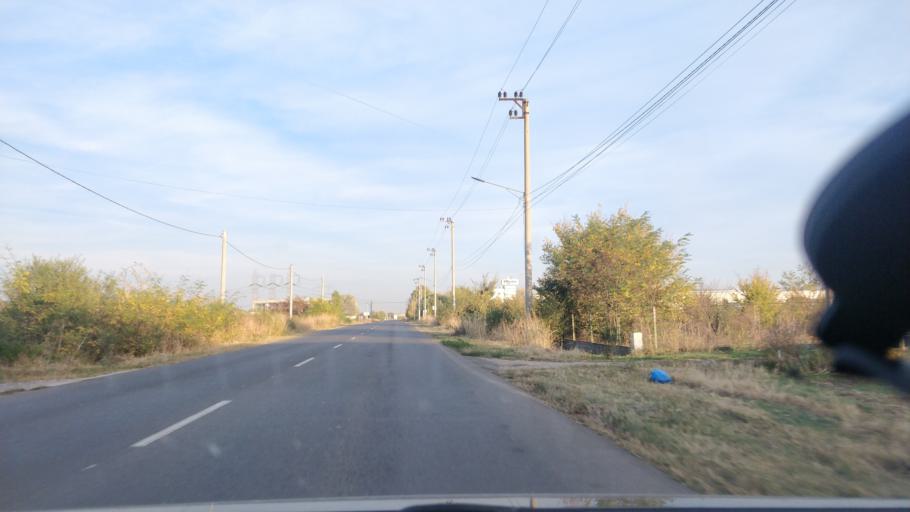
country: RO
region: Ilfov
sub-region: Comuna Ciorogarla
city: Ciorogarla
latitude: 44.4410
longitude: 25.9109
